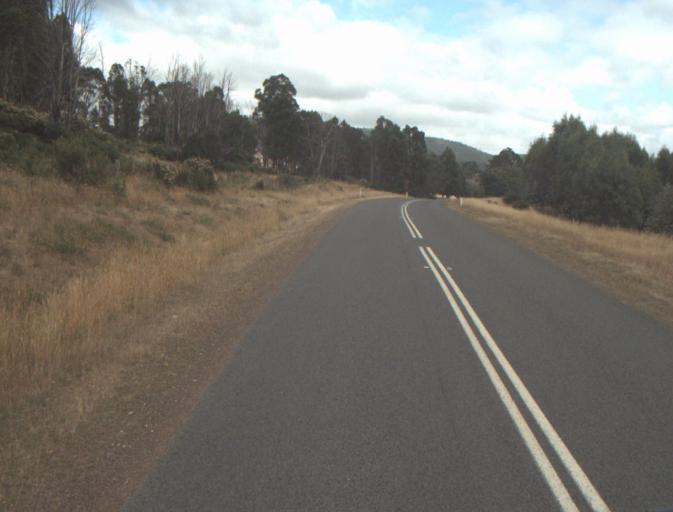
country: AU
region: Tasmania
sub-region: Northern Midlands
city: Evandale
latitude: -41.4805
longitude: 147.5089
